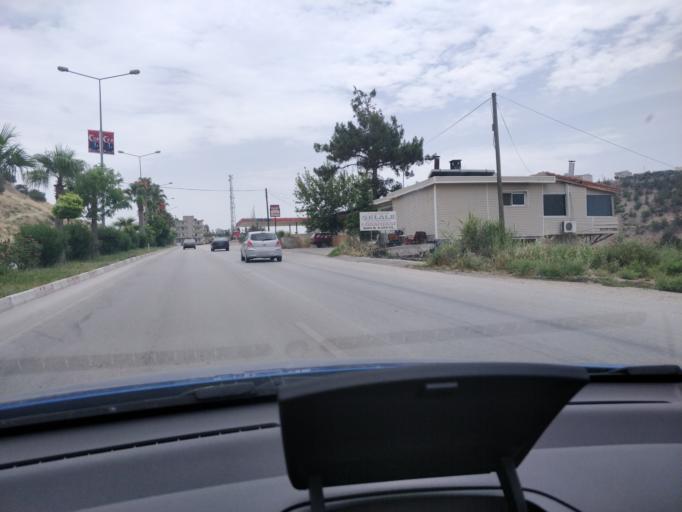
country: TR
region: Mersin
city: Mut
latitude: 36.6487
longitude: 33.4269
